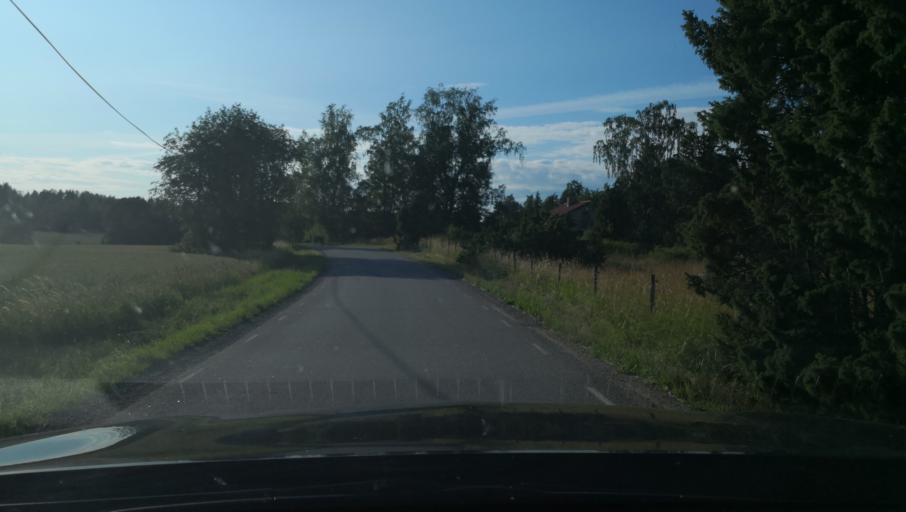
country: SE
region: Uppsala
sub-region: Uppsala Kommun
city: Vattholma
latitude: 59.9311
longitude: 17.8313
